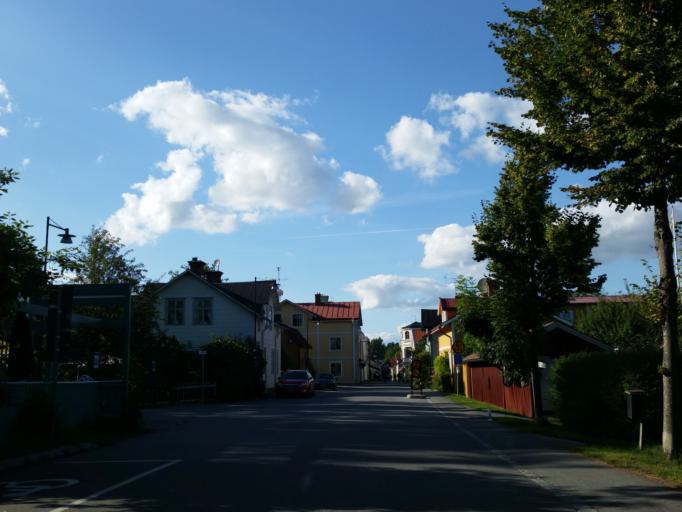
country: SE
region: Soedermanland
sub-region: Trosa Kommun
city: Trosa
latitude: 58.8950
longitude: 17.5481
